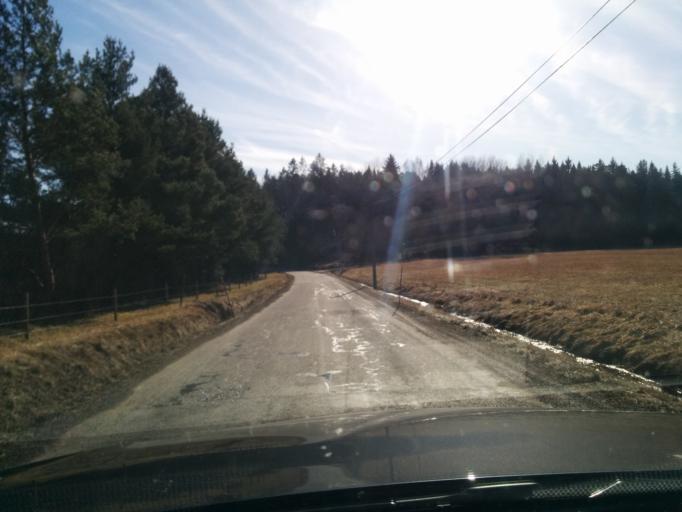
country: SE
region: Stockholm
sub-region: Vallentuna Kommun
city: Vallentuna
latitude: 59.5074
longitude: 18.0089
